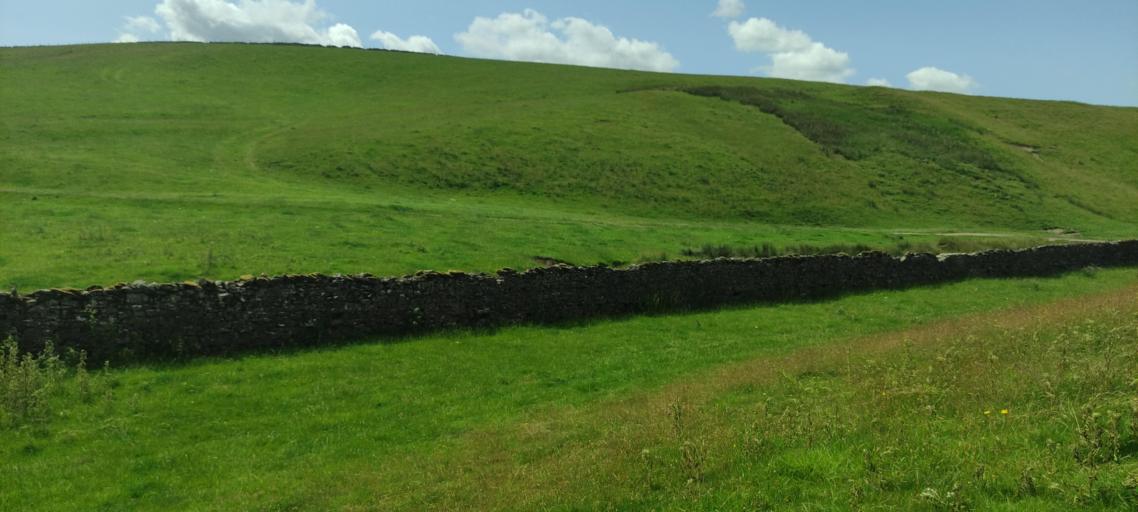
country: GB
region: England
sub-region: Cumbria
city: Kirkby Stephen
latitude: 54.4402
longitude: -2.4356
